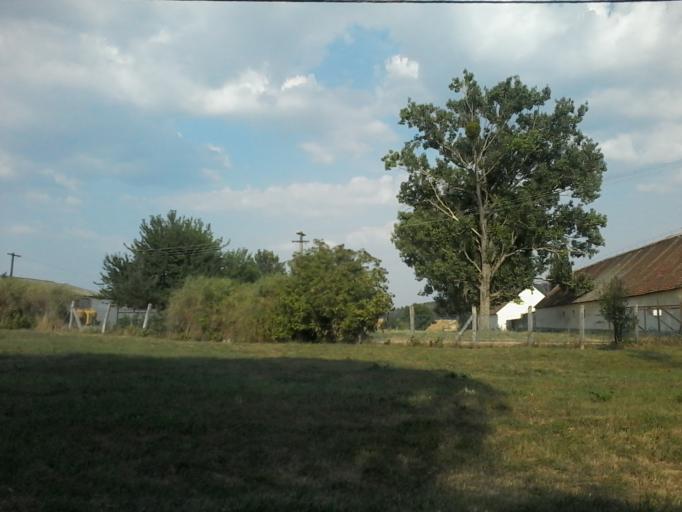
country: HU
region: Vas
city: Celldomolk
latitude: 47.2323
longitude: 17.0885
